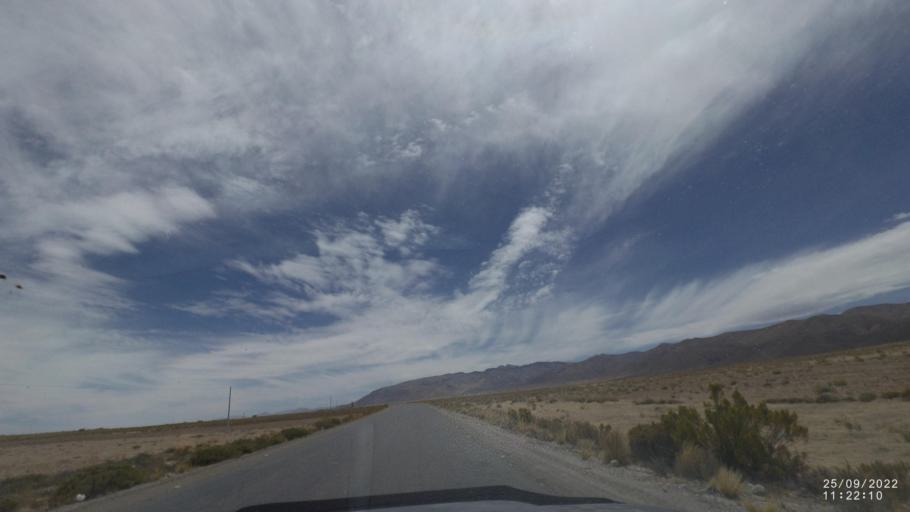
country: BO
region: Oruro
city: Challapata
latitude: -19.1303
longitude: -66.7685
